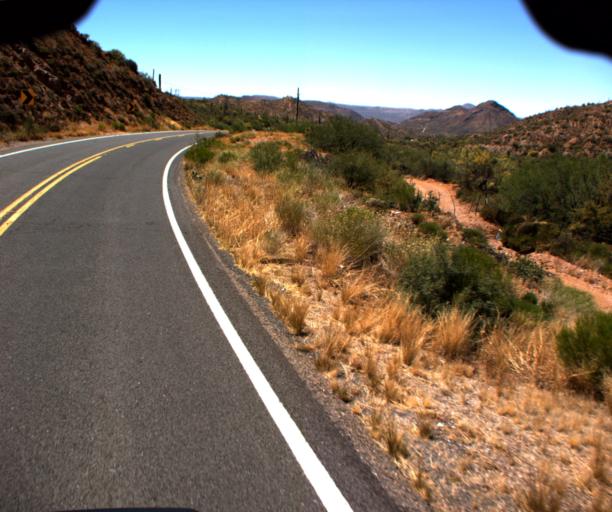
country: US
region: Arizona
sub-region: Pinal County
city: Superior
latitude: 33.1919
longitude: -111.0443
